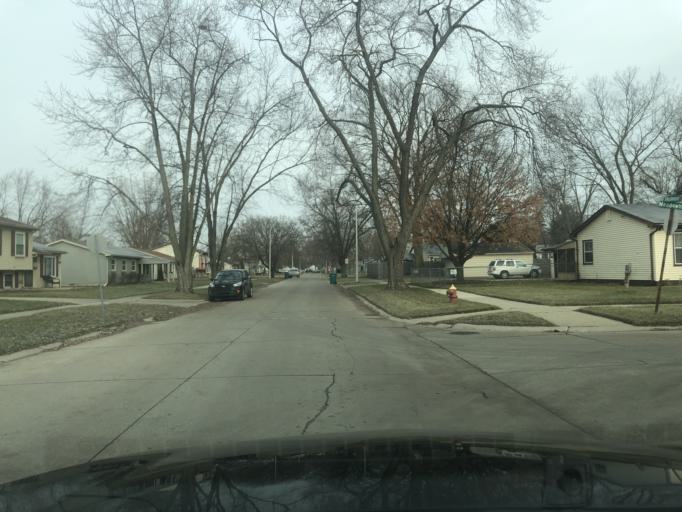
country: US
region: Michigan
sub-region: Wayne County
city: Taylor
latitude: 42.1904
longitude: -83.3146
